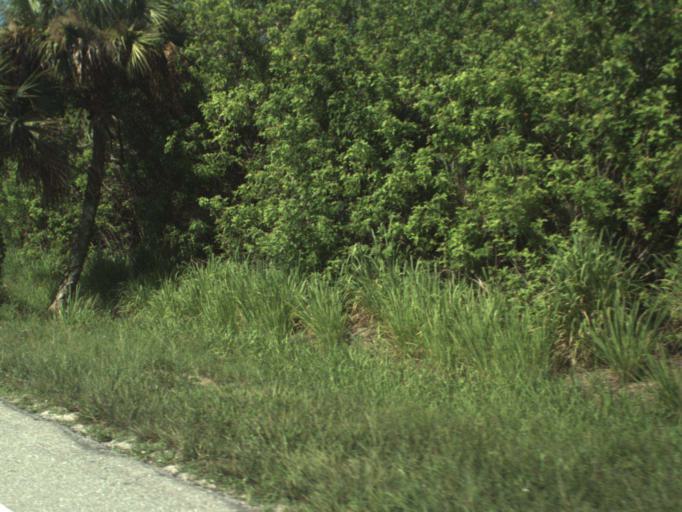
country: US
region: Florida
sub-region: Indian River County
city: Gifford
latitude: 27.6889
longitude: -80.4462
